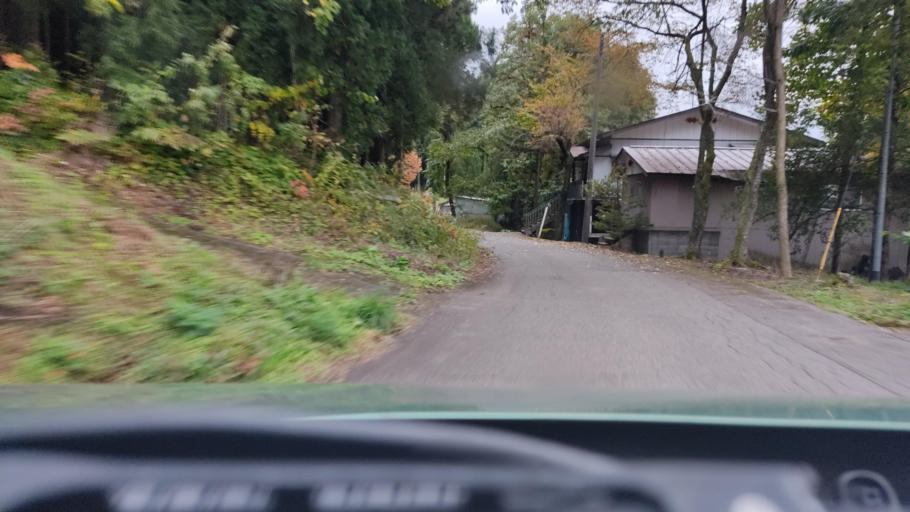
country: JP
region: Akita
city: Kakunodatemachi
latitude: 39.5490
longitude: 140.6232
